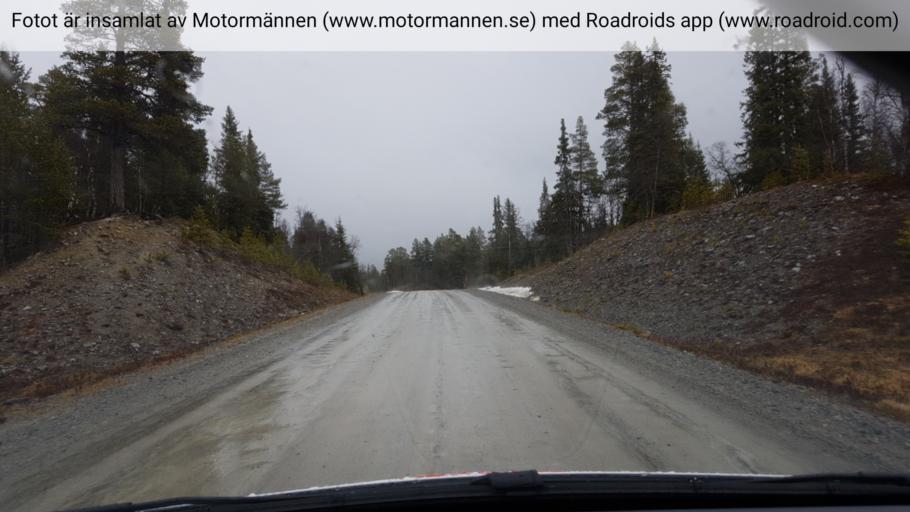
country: SE
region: Jaemtland
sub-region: Are Kommun
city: Are
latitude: 62.6652
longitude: 12.9305
